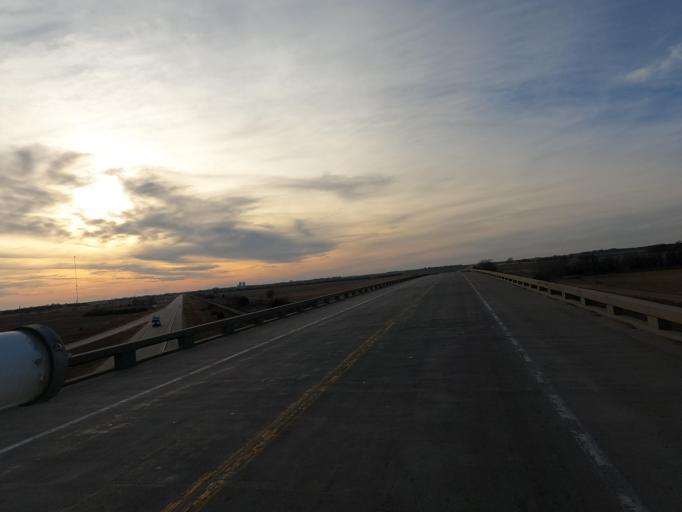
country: US
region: Kansas
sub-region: Reno County
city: South Hutchinson
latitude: 37.9847
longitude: -98.0566
